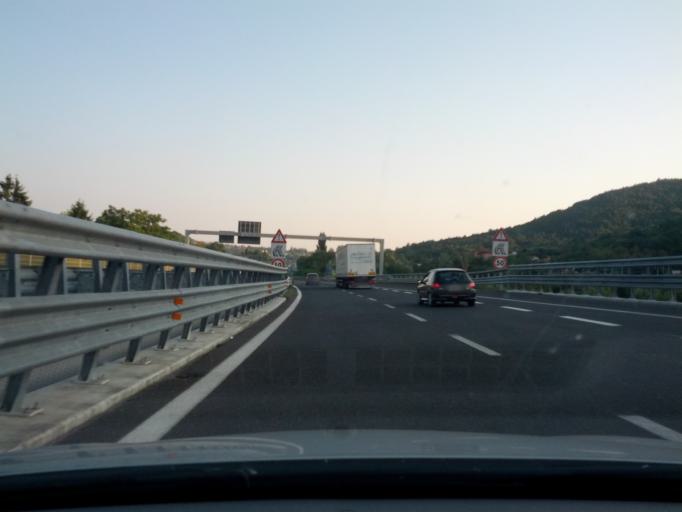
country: SI
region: Koper-Capodistria
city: Spodnje Skofije
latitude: 45.5872
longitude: 13.7982
